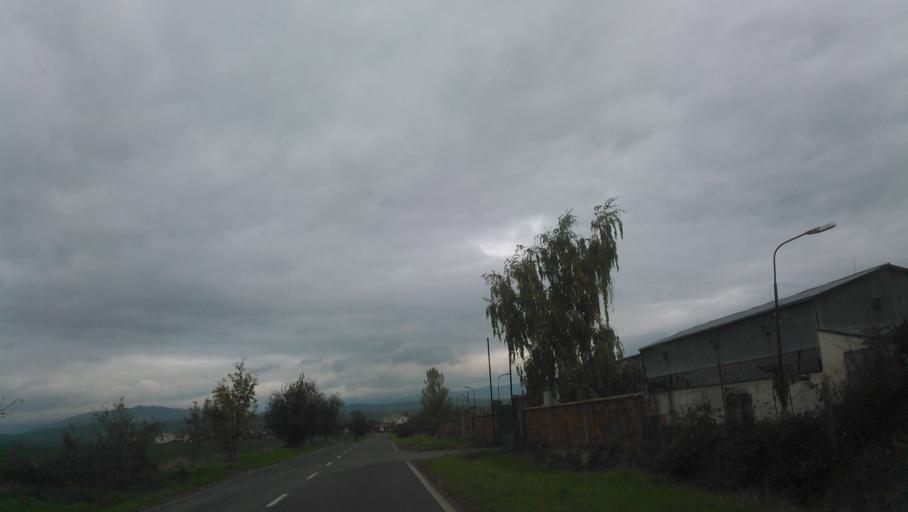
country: SK
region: Banskobystricky
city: Lucenec
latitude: 48.3825
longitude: 19.7053
